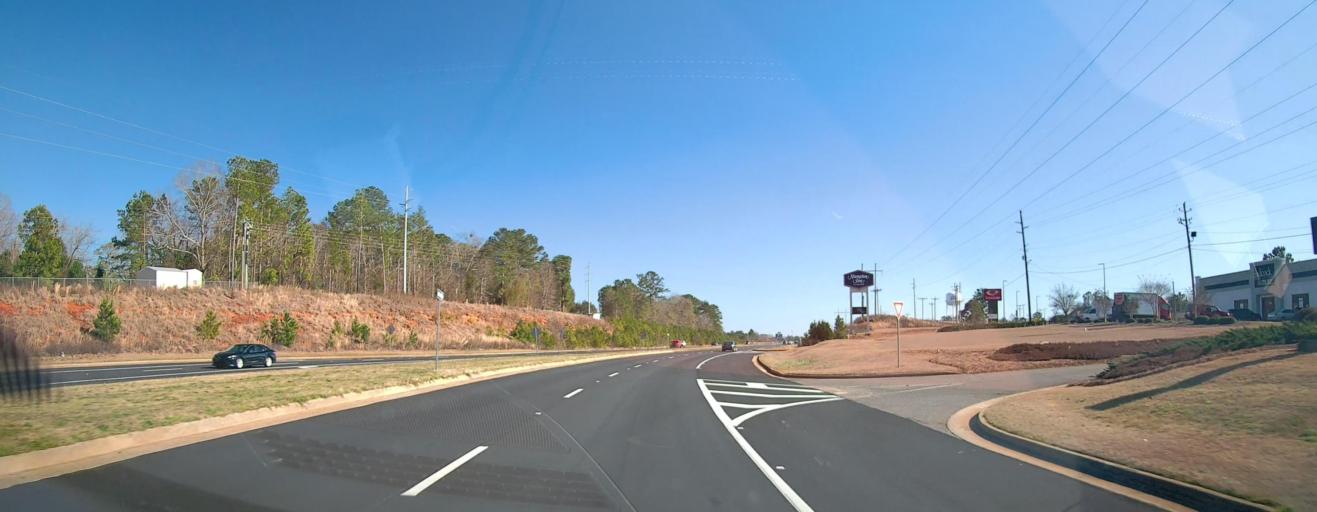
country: US
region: Georgia
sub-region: Sumter County
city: Americus
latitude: 32.0701
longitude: -84.2072
